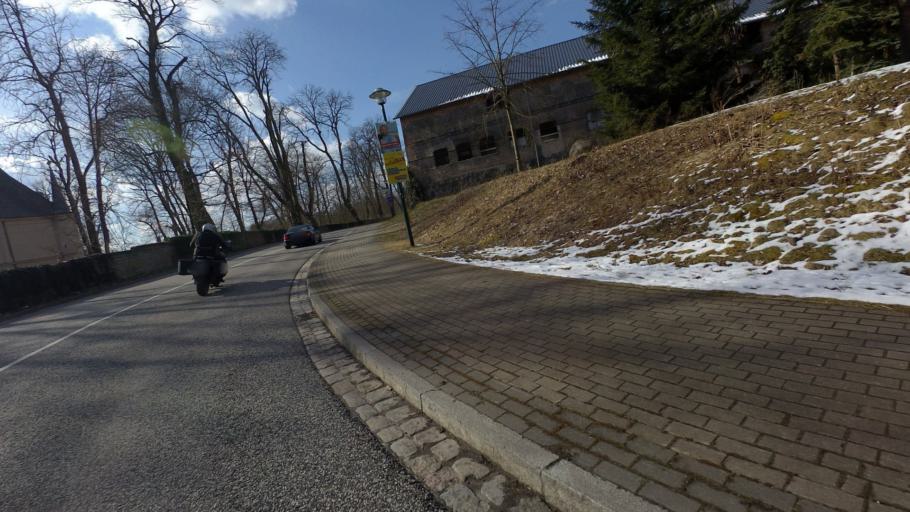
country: DE
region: Brandenburg
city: Rudnitz
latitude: 52.7600
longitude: 13.5666
